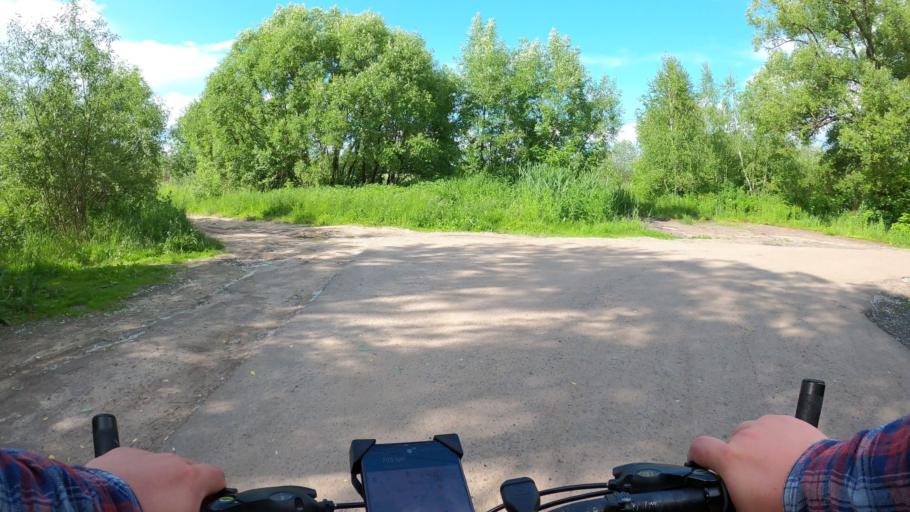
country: RU
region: Moskovskaya
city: Konobeyevo
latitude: 55.4154
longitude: 38.6561
